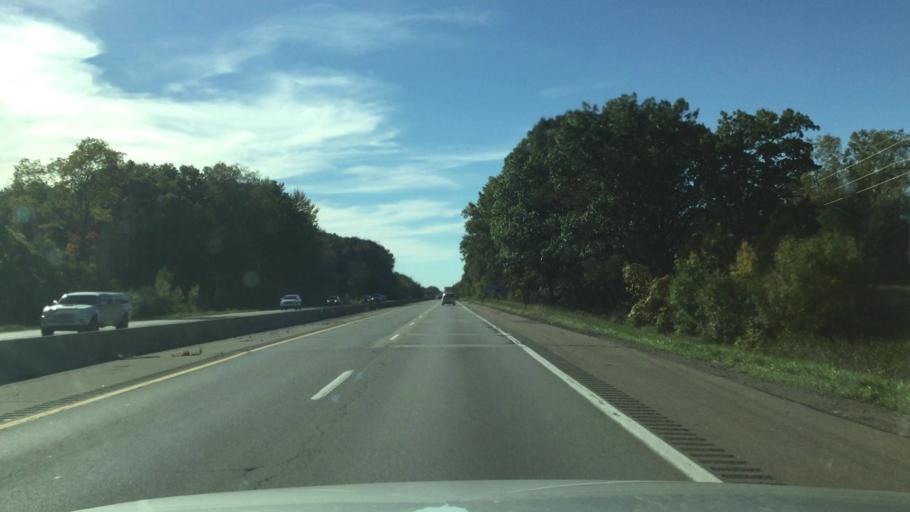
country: US
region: Michigan
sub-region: Jackson County
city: Spring Arbor
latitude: 42.2691
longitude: -84.5184
